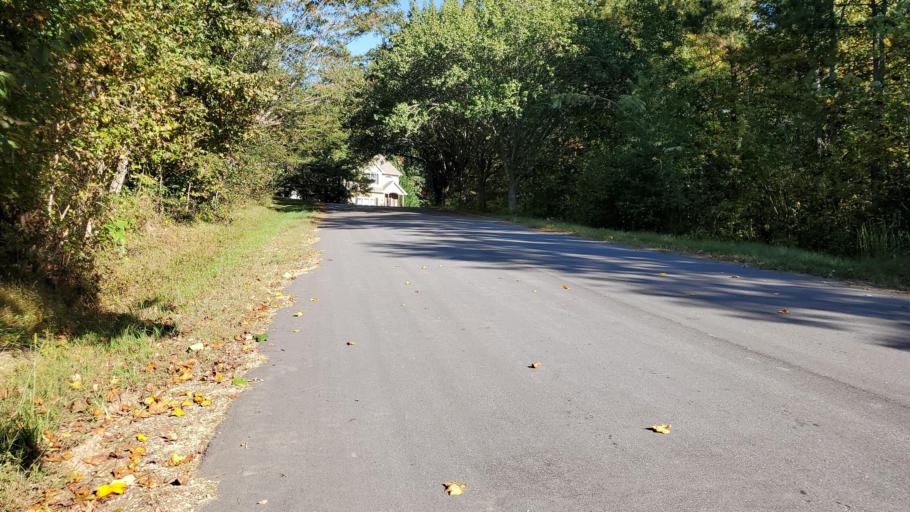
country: US
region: South Carolina
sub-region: Greenville County
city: Tigerville
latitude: 35.0724
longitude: -82.3096
